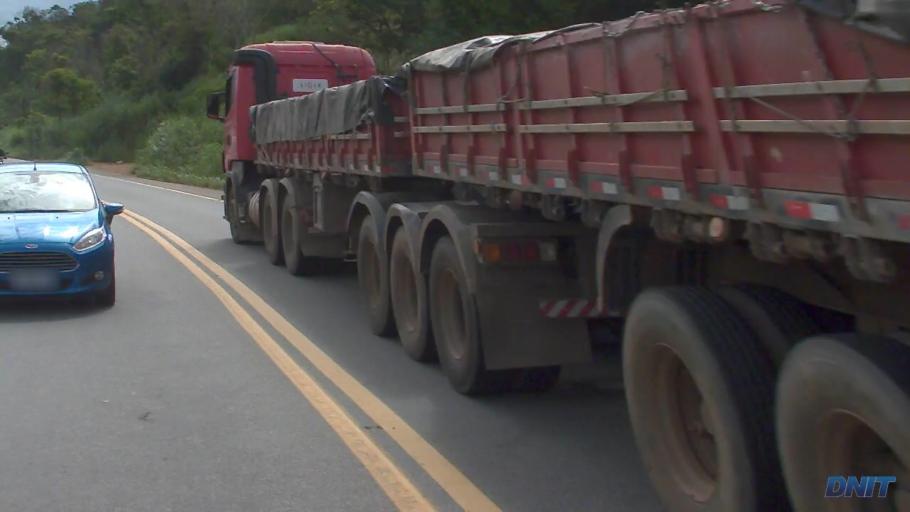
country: BR
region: Minas Gerais
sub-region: Ipaba
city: Ipaba
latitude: -19.3641
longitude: -42.4489
